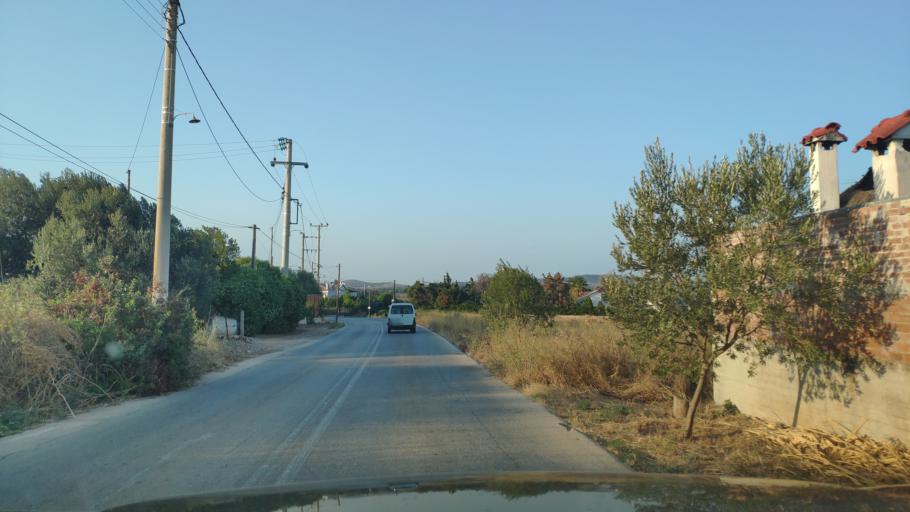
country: GR
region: Attica
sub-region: Nomarchia Anatolikis Attikis
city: Markopoulo
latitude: 37.9062
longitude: 23.9615
